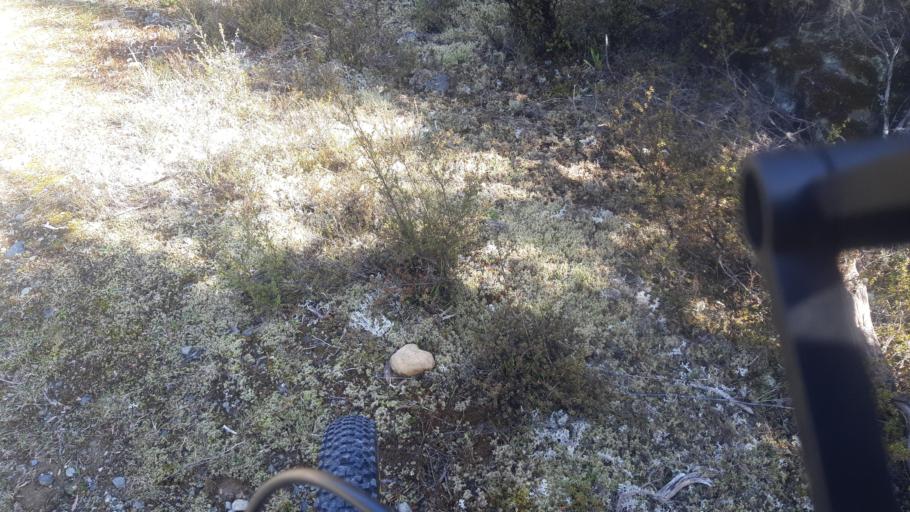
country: NZ
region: Tasman
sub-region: Tasman District
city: Wakefield
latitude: -41.8028
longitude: 172.8414
